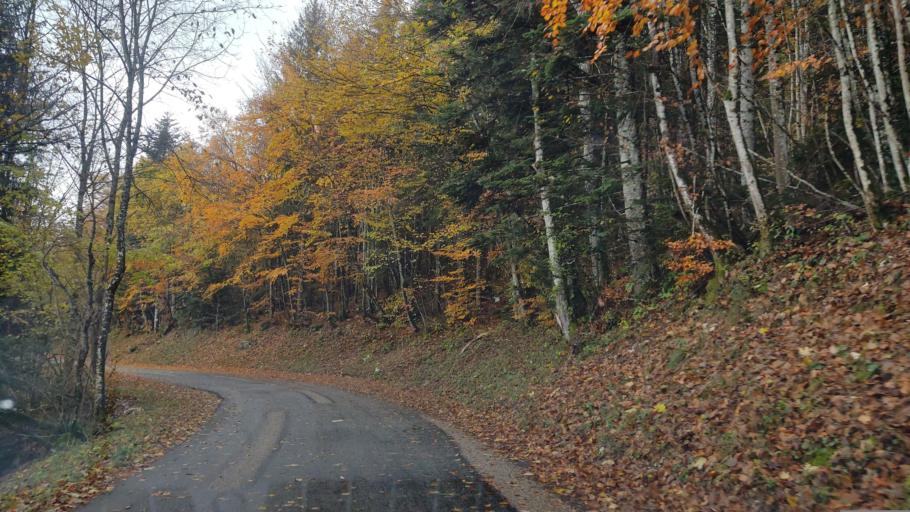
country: FR
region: Rhone-Alpes
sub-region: Departement de la Savoie
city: Le Bourget-du-Lac
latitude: 45.6611
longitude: 5.8367
